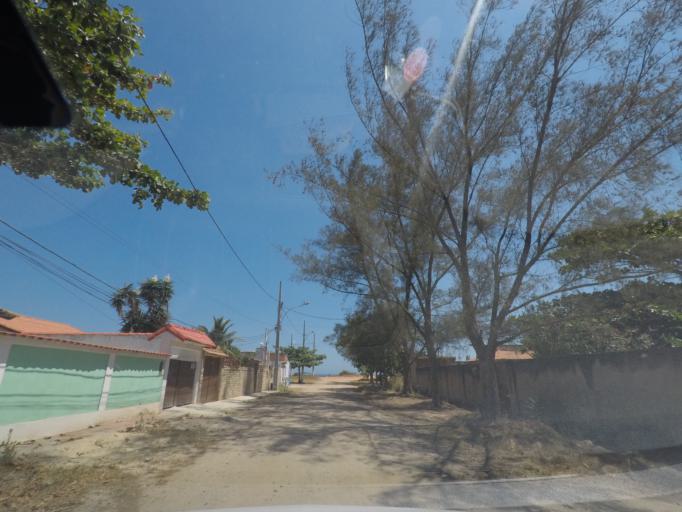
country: BR
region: Rio de Janeiro
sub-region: Marica
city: Marica
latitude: -22.9725
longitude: -42.9325
